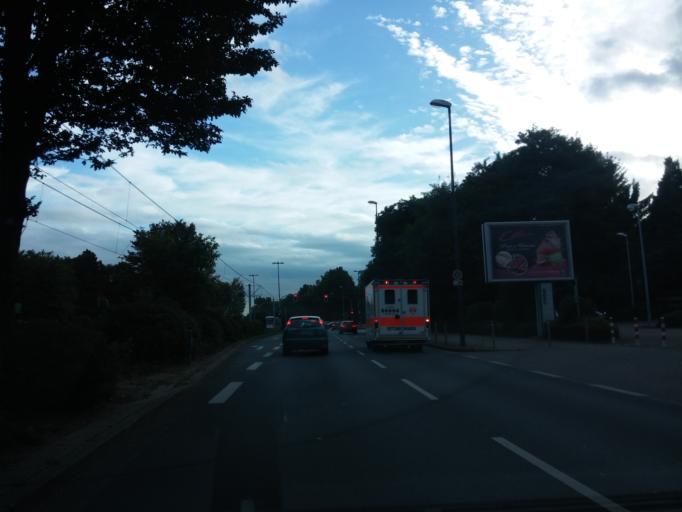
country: DE
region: North Rhine-Westphalia
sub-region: Regierungsbezirk Munster
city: Gladbeck
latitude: 51.5743
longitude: 7.0575
